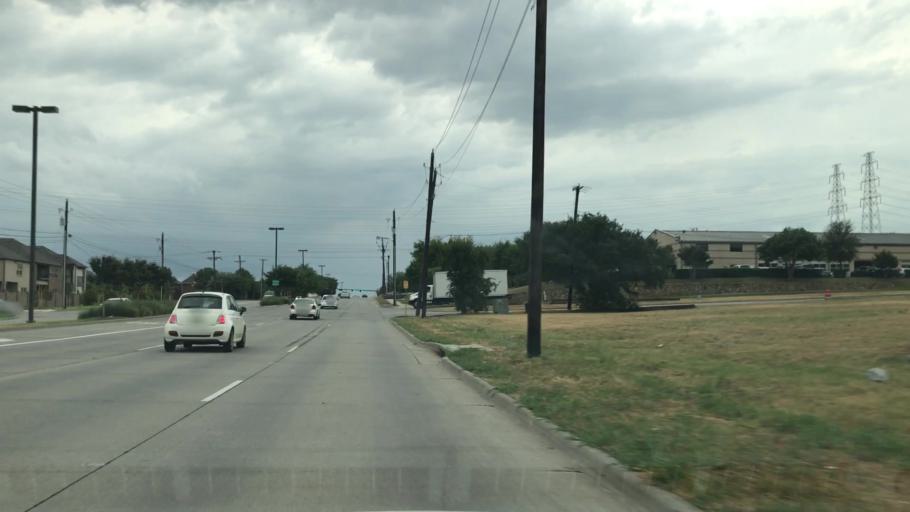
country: US
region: Texas
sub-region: Dallas County
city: Carrollton
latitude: 32.9791
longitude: -96.9100
